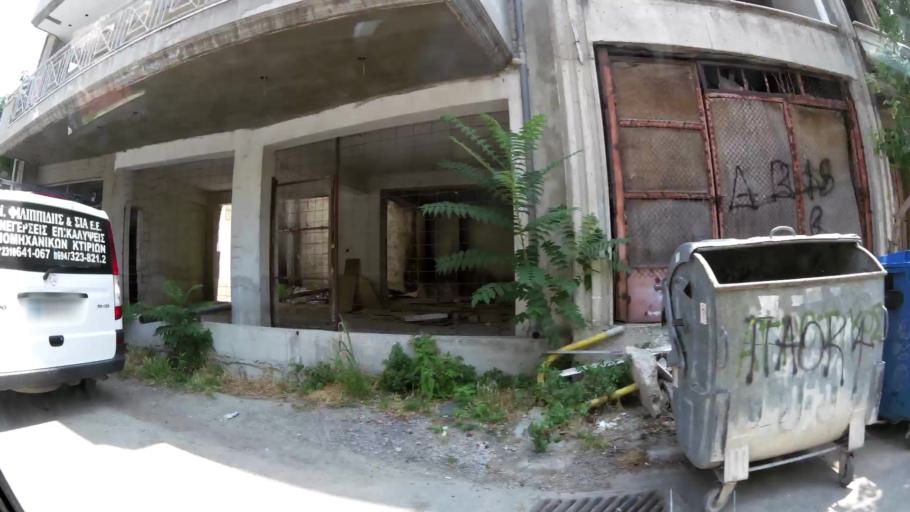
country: GR
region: Central Macedonia
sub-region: Nomos Thessalonikis
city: Evosmos
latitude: 40.6667
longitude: 22.9099
